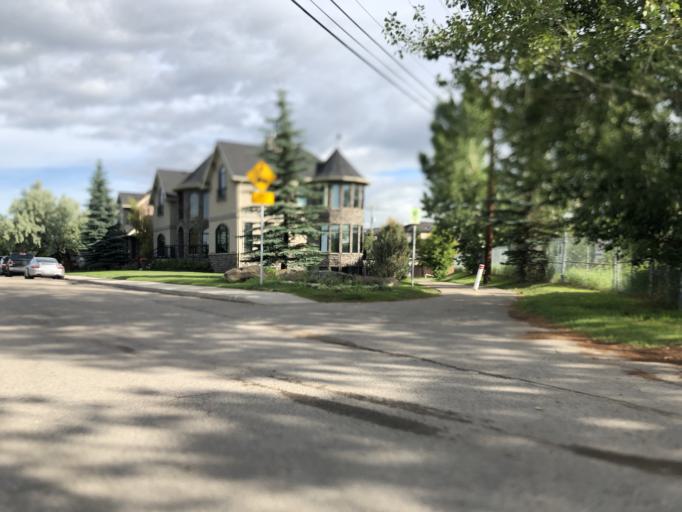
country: CA
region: Alberta
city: Calgary
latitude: 51.0314
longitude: -114.0114
